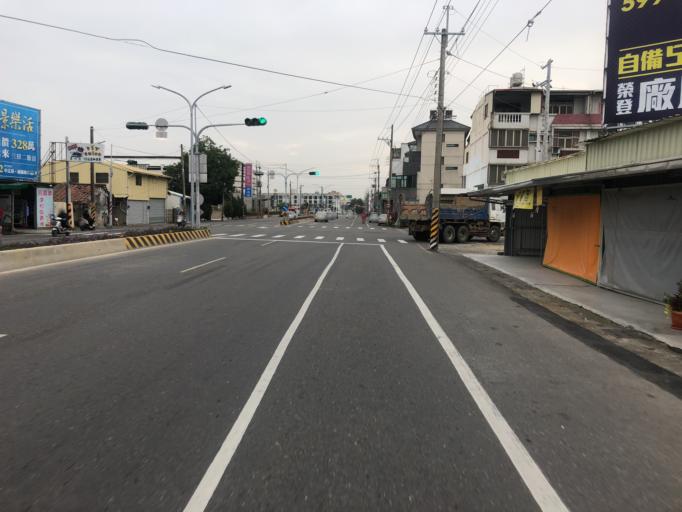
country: TW
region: Taiwan
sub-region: Tainan
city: Tainan
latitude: 23.1382
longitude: 120.2884
